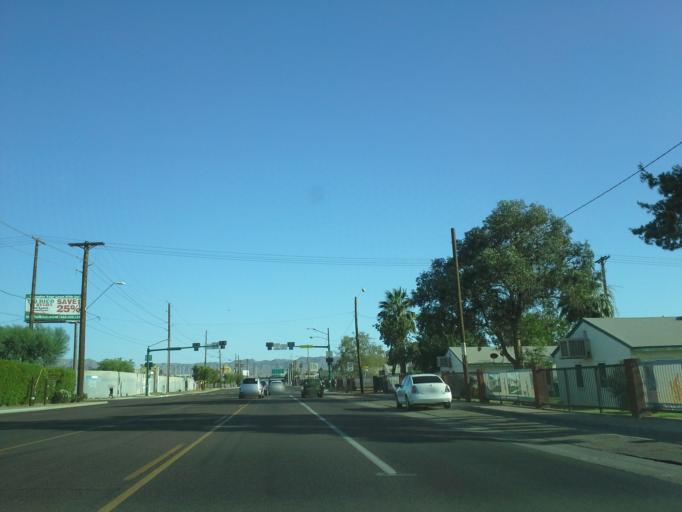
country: US
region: Arizona
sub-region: Maricopa County
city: Phoenix
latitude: 33.4338
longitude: -112.1000
